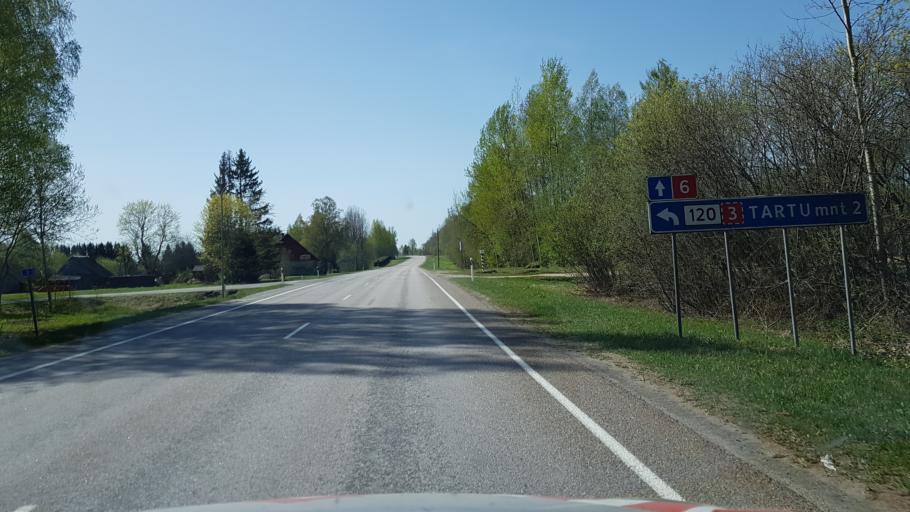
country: EE
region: Valgamaa
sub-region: Valga linn
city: Valga
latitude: 57.8066
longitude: 26.0395
